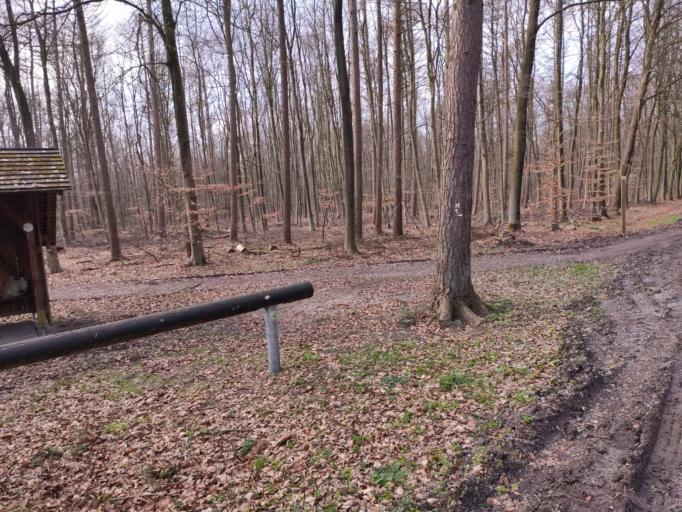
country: DE
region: North Rhine-Westphalia
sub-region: Regierungsbezirk Munster
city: Klein Reken
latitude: 51.7660
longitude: 7.0857
